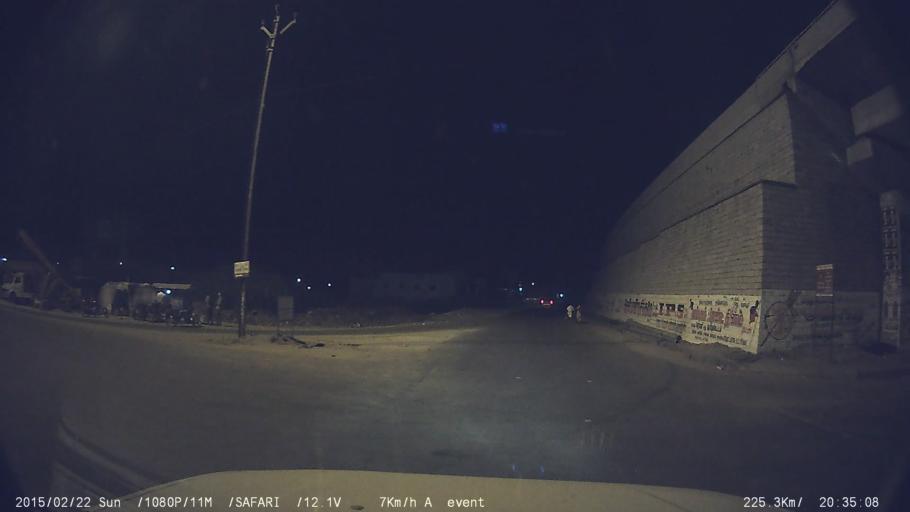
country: IN
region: Tamil Nadu
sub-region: Dindigul
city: Dindigul
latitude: 10.3722
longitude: 77.9517
